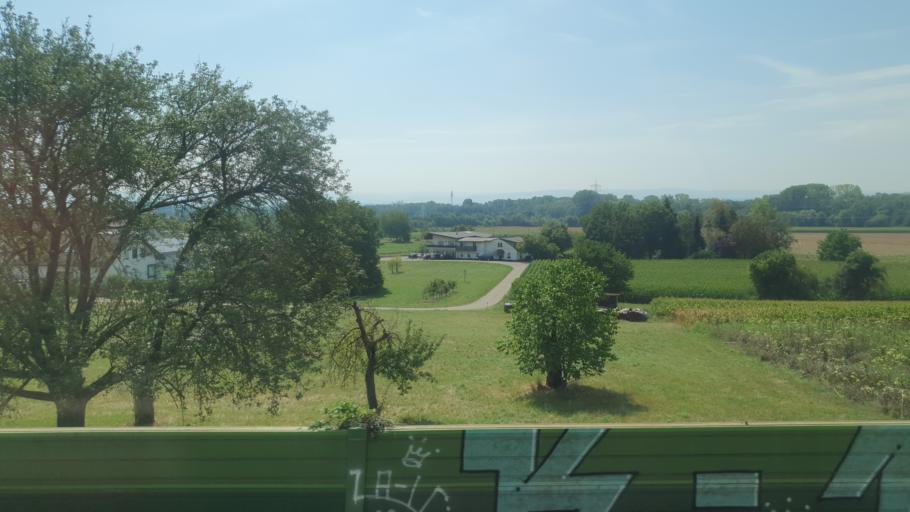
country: DE
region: Baden-Wuerttemberg
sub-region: Freiburg Region
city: Efringen-Kirchen
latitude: 47.6569
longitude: 7.5565
